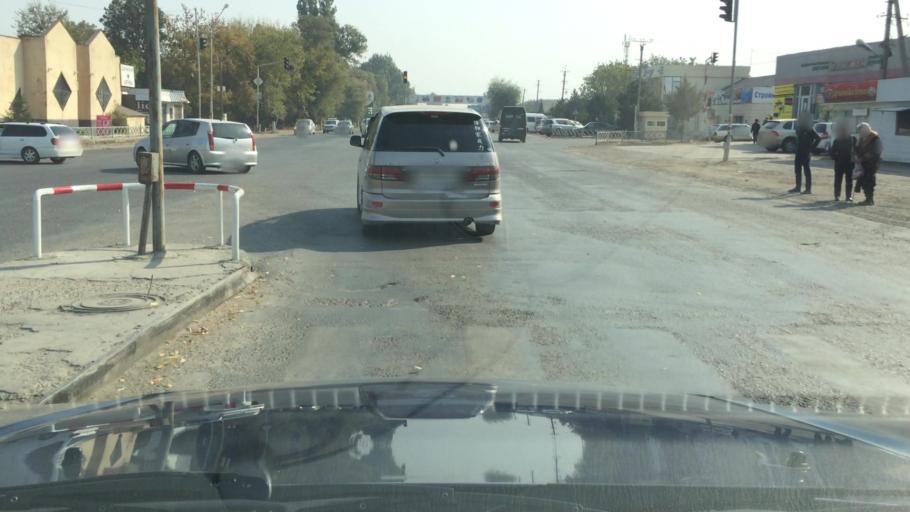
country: KG
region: Chuy
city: Lebedinovka
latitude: 42.8857
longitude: 74.6782
